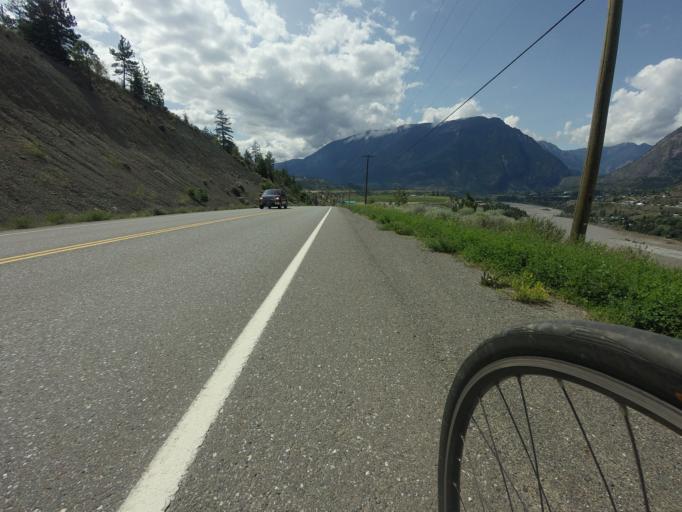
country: CA
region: British Columbia
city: Lillooet
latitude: 50.7096
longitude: -121.9085
